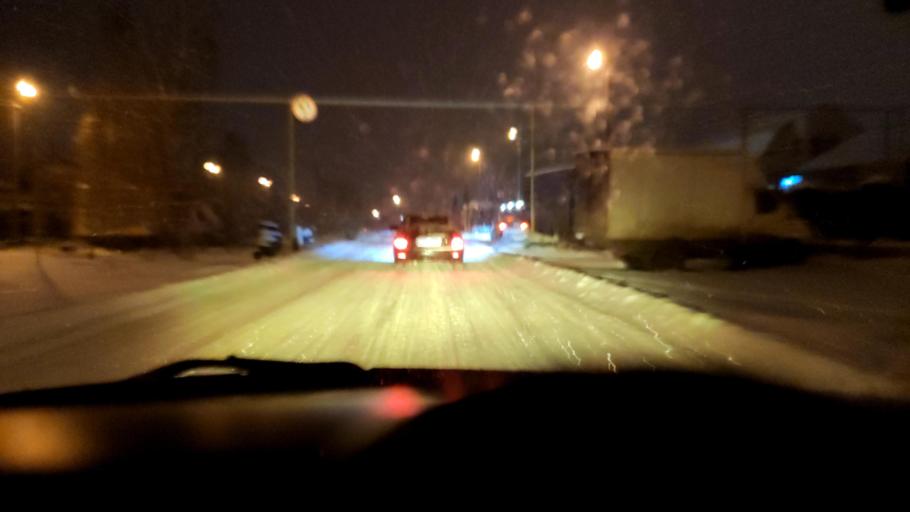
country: RU
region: Voronezj
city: Pridonskoy
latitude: 51.6735
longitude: 39.0771
